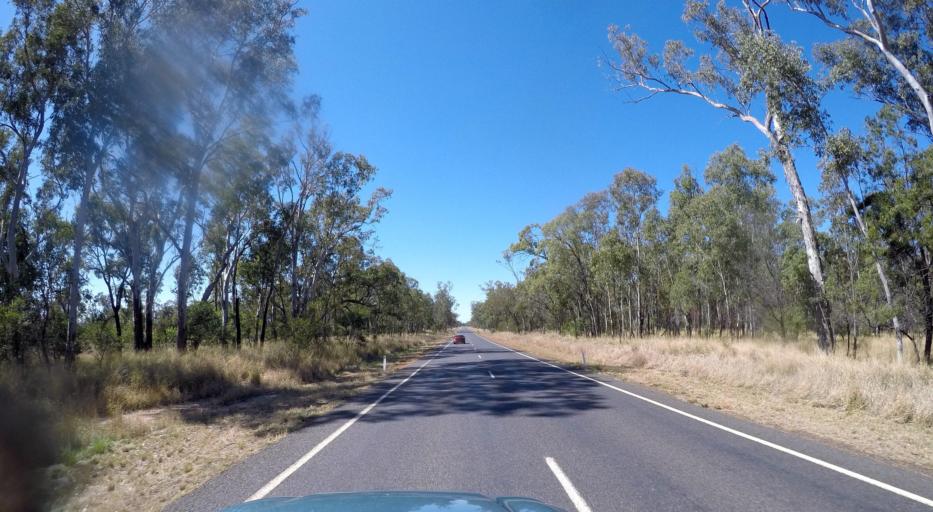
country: AU
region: Queensland
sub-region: Western Downs
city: Westcourt
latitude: -26.5231
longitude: 150.1172
